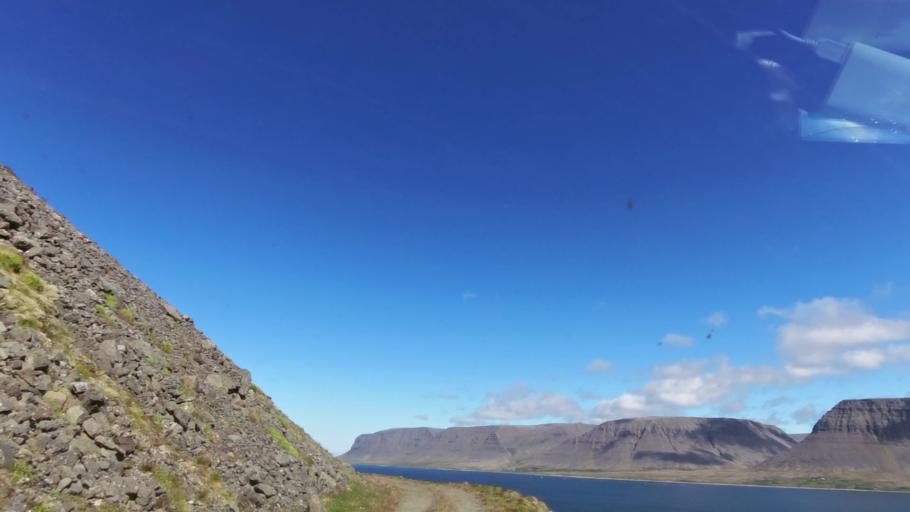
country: IS
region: West
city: Olafsvik
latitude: 65.6322
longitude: -23.9170
